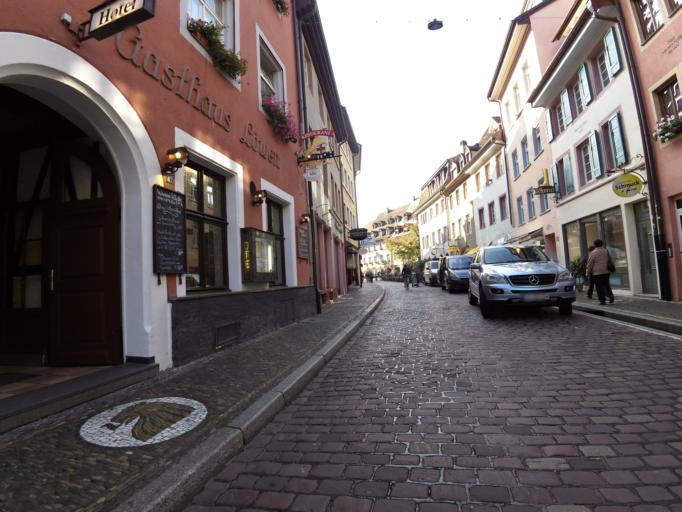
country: DE
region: Baden-Wuerttemberg
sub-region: Freiburg Region
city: Freiburg
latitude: 47.9944
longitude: 7.8538
